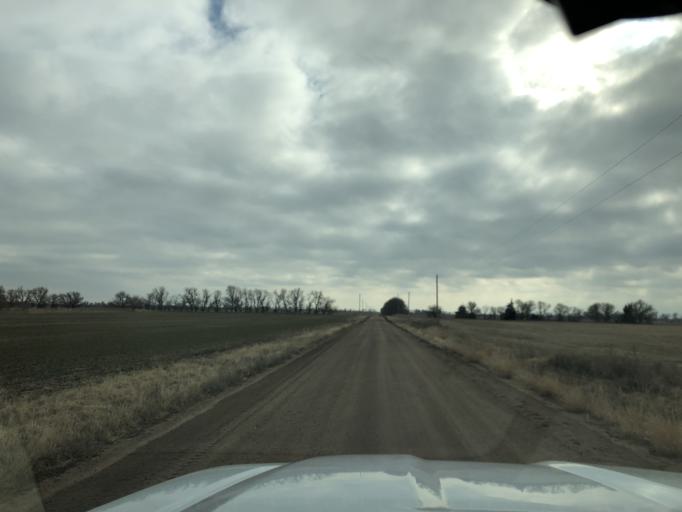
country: US
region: Kansas
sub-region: Reno County
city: Nickerson
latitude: 38.0384
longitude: -98.2158
